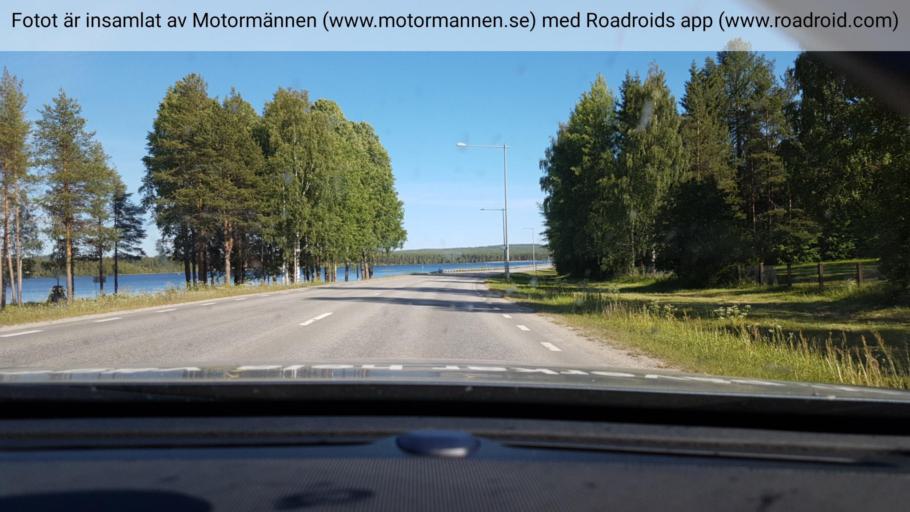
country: SE
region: Vaesterbotten
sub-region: Lycksele Kommun
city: Lycksele
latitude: 64.6031
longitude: 18.6717
